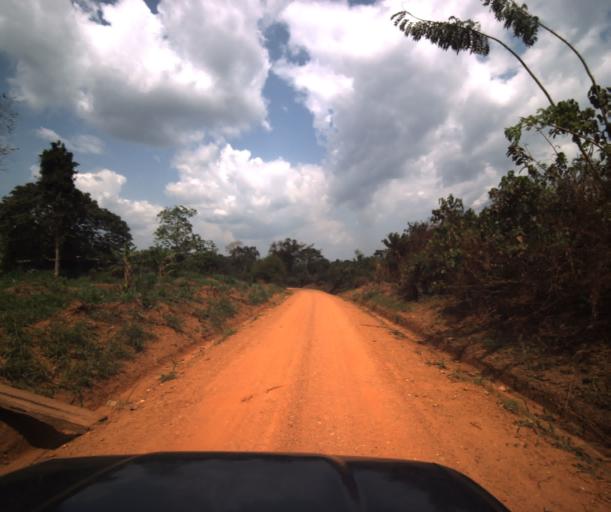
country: CM
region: Centre
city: Akono
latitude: 3.5583
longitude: 11.0771
